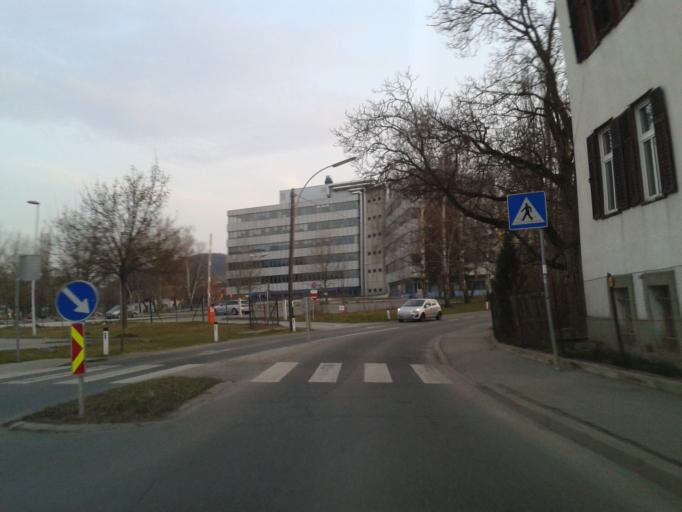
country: AT
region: Styria
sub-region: Politischer Bezirk Graz-Umgebung
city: Stattegg
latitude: 47.1100
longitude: 15.4228
